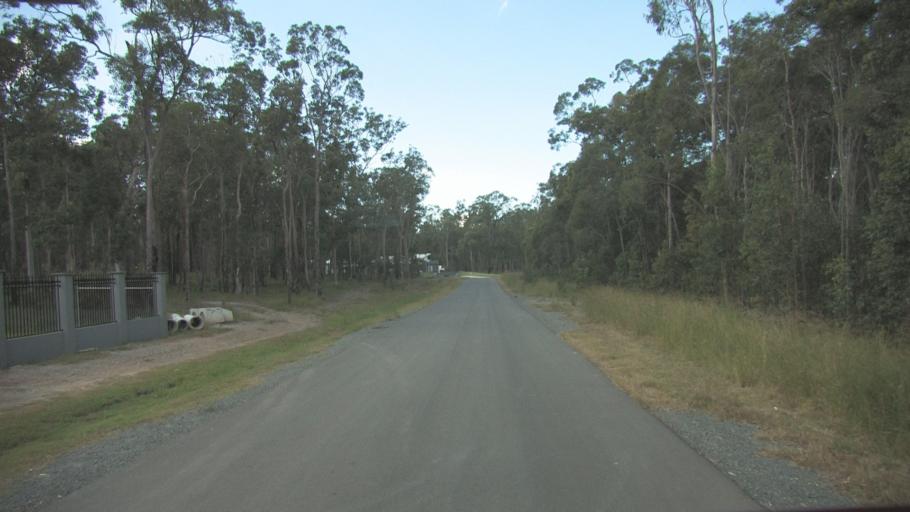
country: AU
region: Queensland
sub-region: Gold Coast
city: Yatala
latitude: -27.6672
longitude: 153.2473
